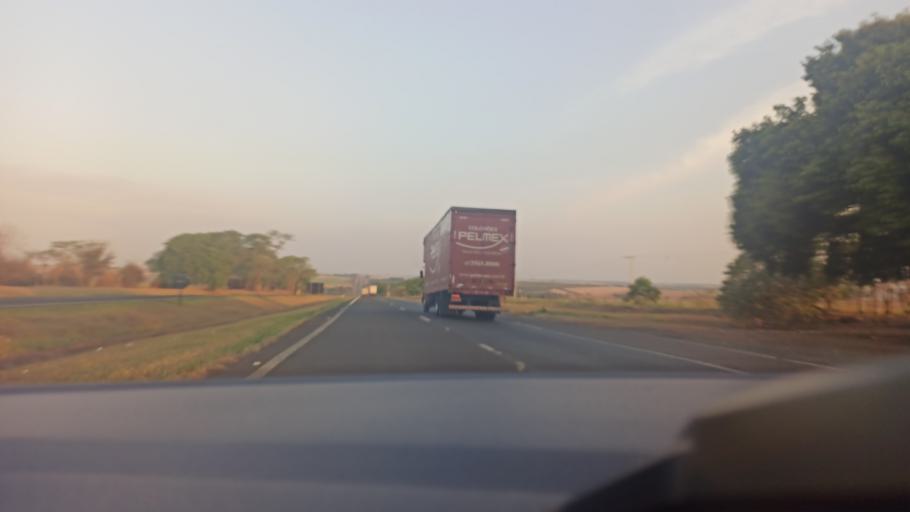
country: BR
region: Sao Paulo
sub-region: Santa Adelia
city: Santa Adelia
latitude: -21.3858
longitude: -48.7283
